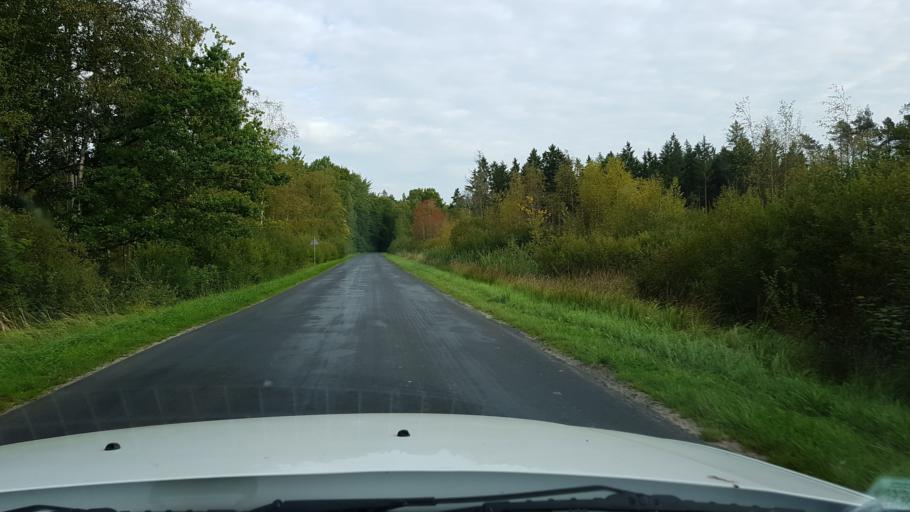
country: PL
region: West Pomeranian Voivodeship
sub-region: Powiat slawienski
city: Slawno
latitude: 54.4030
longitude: 16.6155
